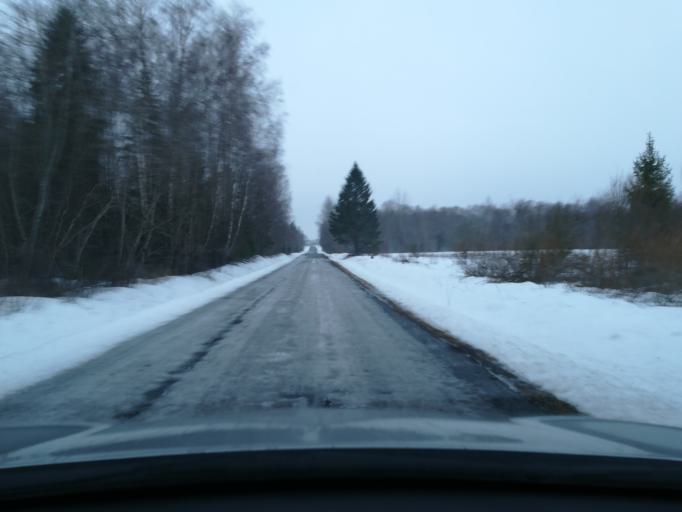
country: EE
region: Harju
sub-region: Raasiku vald
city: Raasiku
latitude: 59.3421
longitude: 25.2453
